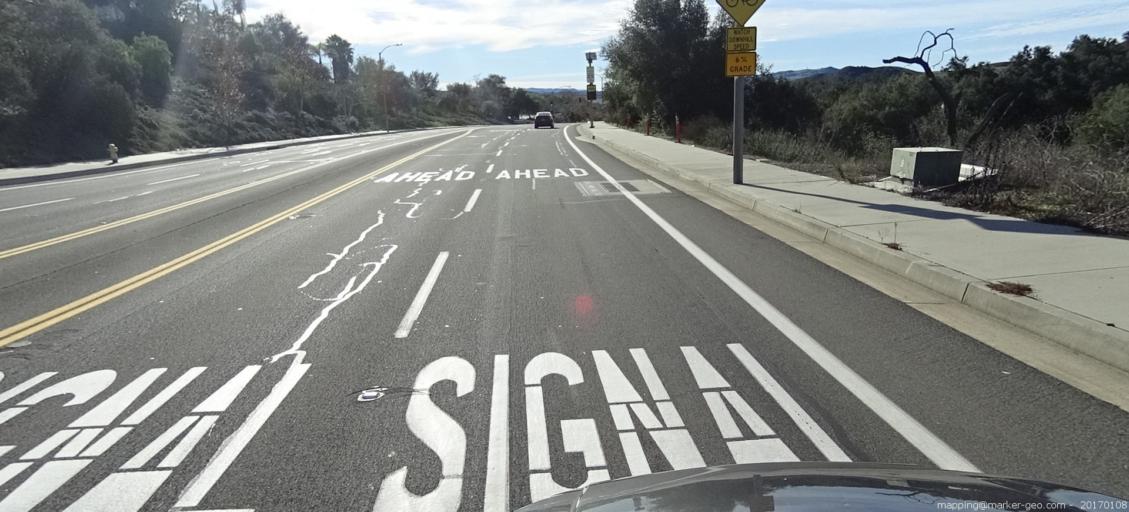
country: US
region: California
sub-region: Orange County
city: Coto De Caza
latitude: 33.5838
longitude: -117.5937
